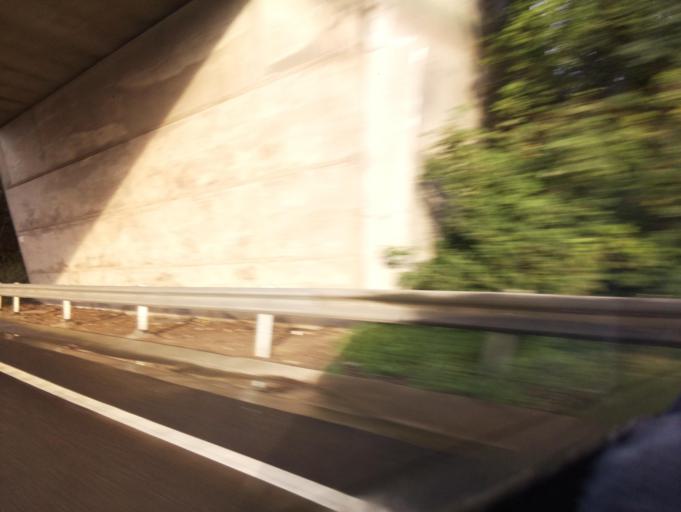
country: GB
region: England
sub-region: Oxfordshire
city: Abingdon
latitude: 51.6781
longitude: -1.3003
